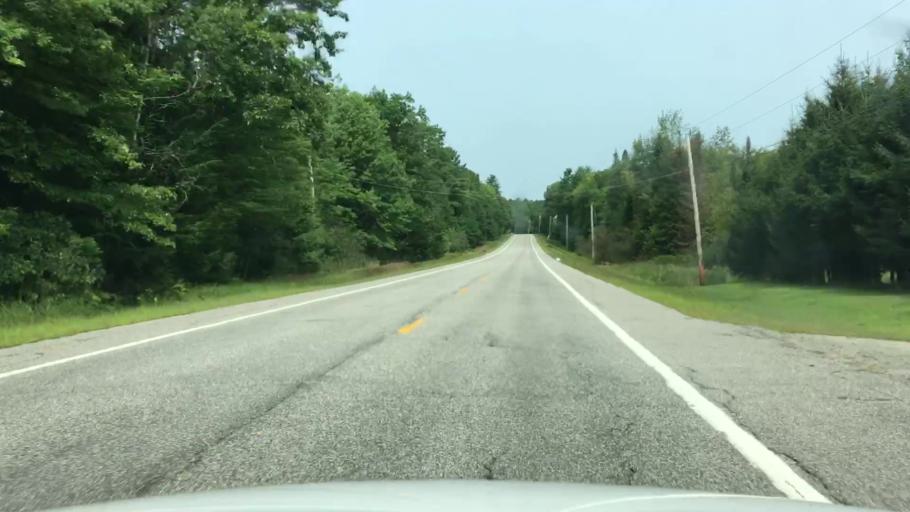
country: US
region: Maine
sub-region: Kennebec County
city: Wayne
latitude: 44.3655
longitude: -70.0891
